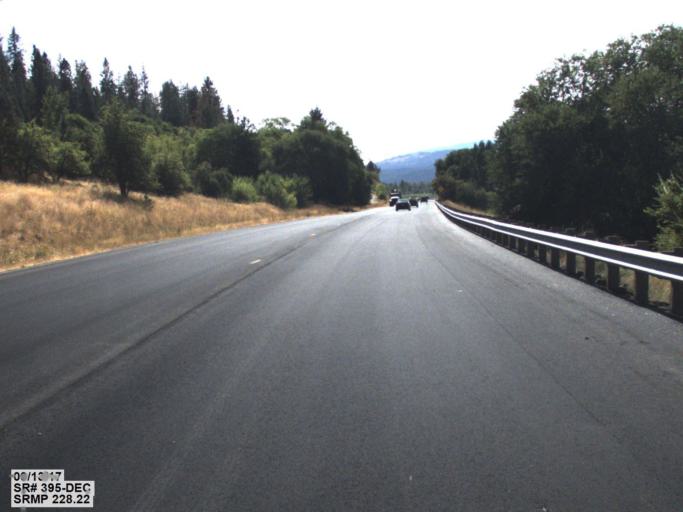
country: US
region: Washington
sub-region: Stevens County
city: Colville
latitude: 48.5262
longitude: -117.9027
